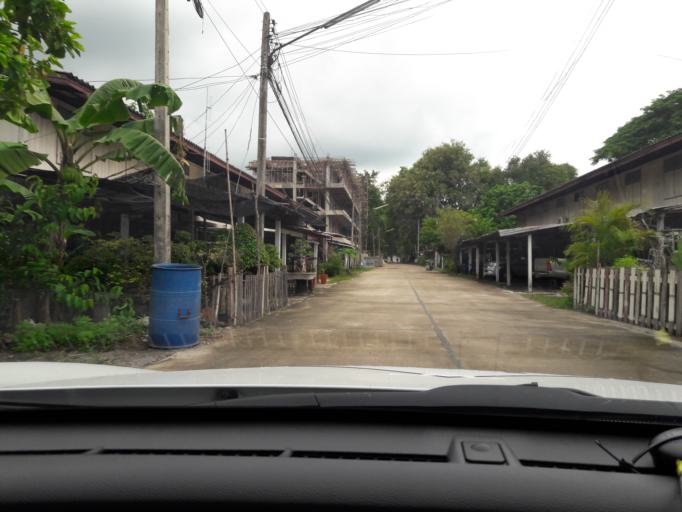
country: TH
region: Nakhon Sawan
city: Tak Fa
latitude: 15.3507
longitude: 100.4944
